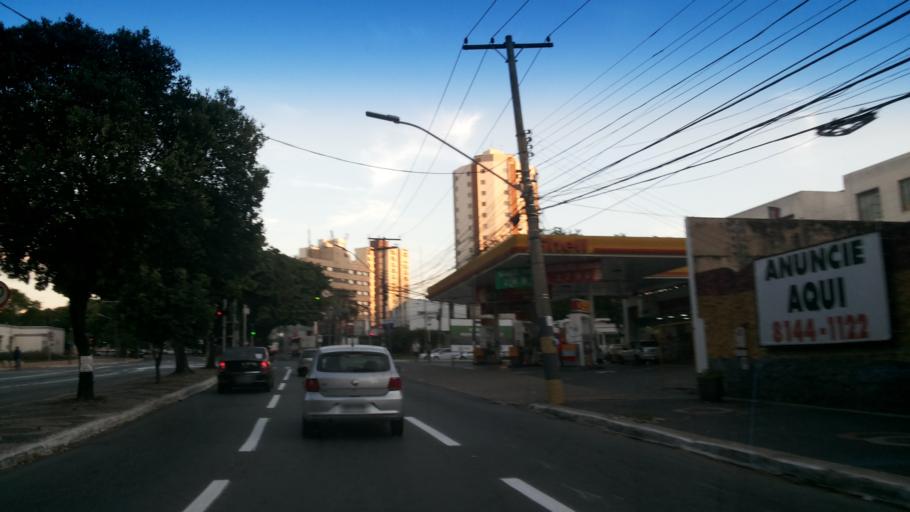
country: BR
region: Goias
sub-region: Goiania
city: Goiania
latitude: -16.6805
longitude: -49.2583
